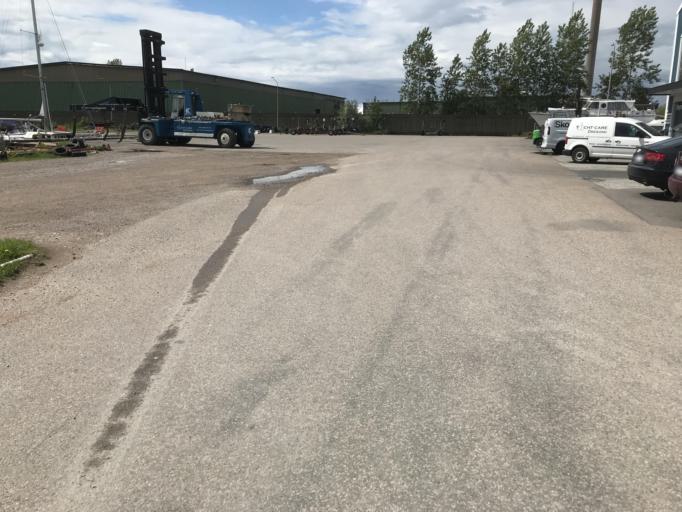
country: SE
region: Skane
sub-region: Landskrona
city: Landskrona
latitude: 55.8616
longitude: 12.8501
